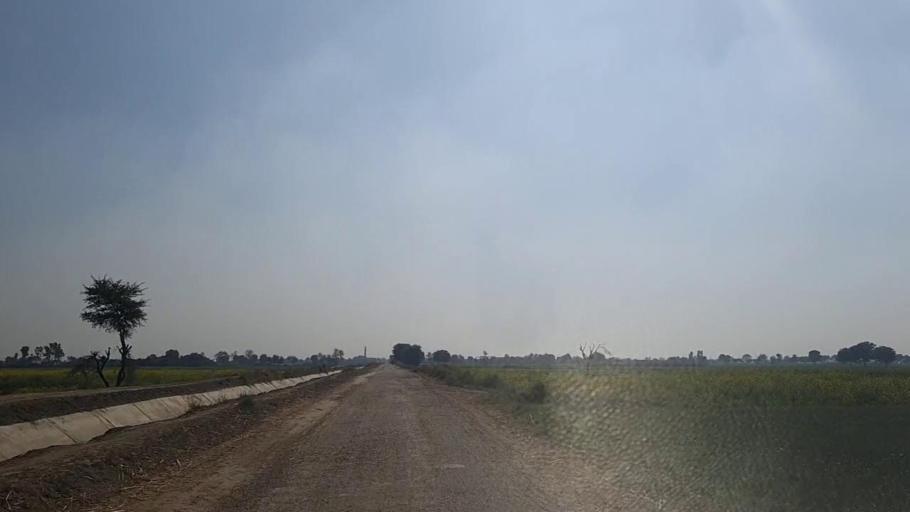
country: PK
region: Sindh
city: Shahpur Chakar
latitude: 26.1983
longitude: 68.5836
